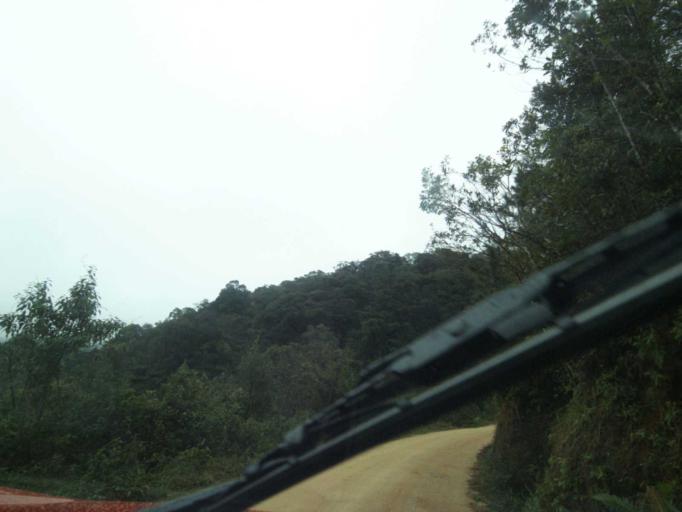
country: BR
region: Santa Catarina
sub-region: Anitapolis
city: Anitapolis
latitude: -27.9223
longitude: -49.1875
